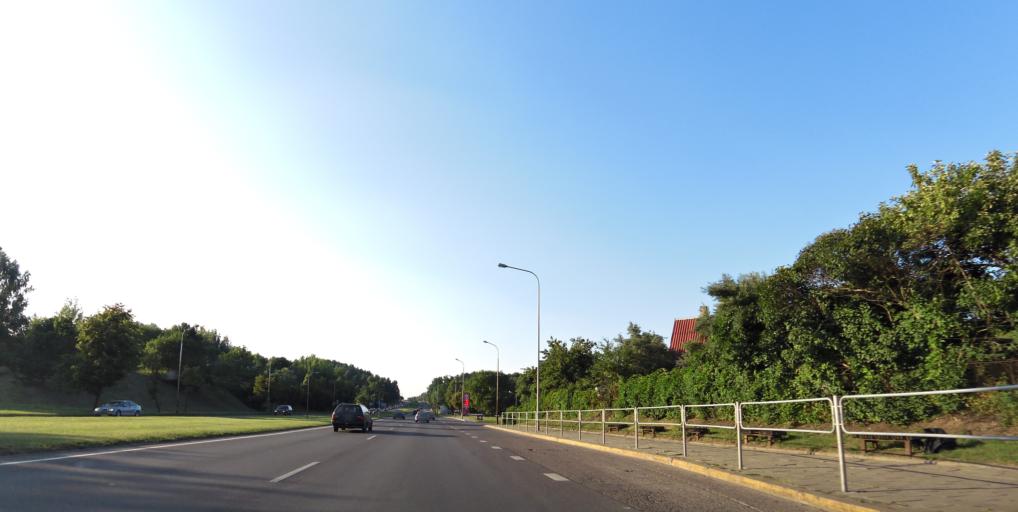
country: LT
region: Vilnius County
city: Seskine
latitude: 54.7212
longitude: 25.2705
